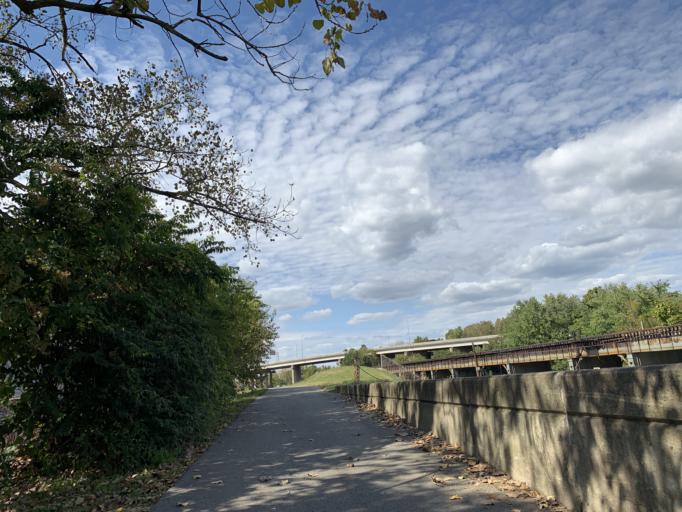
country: US
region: Indiana
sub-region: Floyd County
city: New Albany
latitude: 38.2754
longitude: -85.7975
